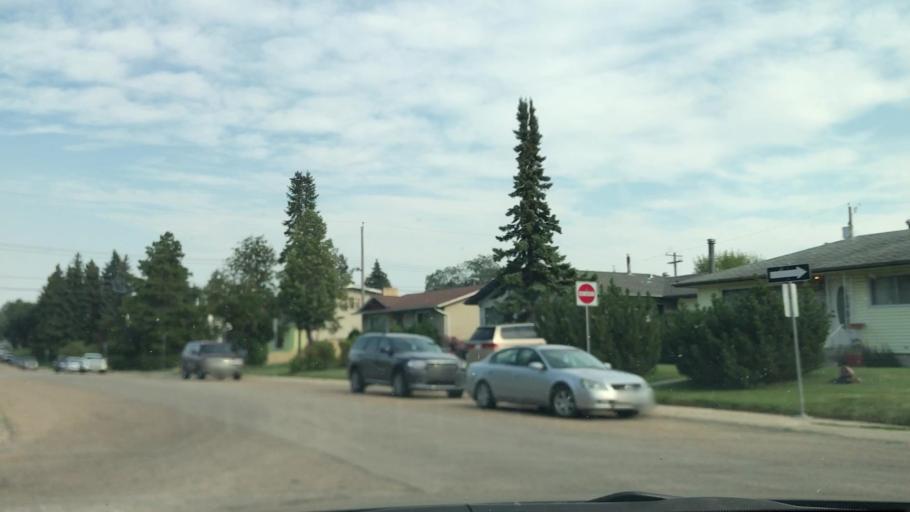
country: CA
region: Alberta
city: Edmonton
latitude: 53.4895
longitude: -113.5121
